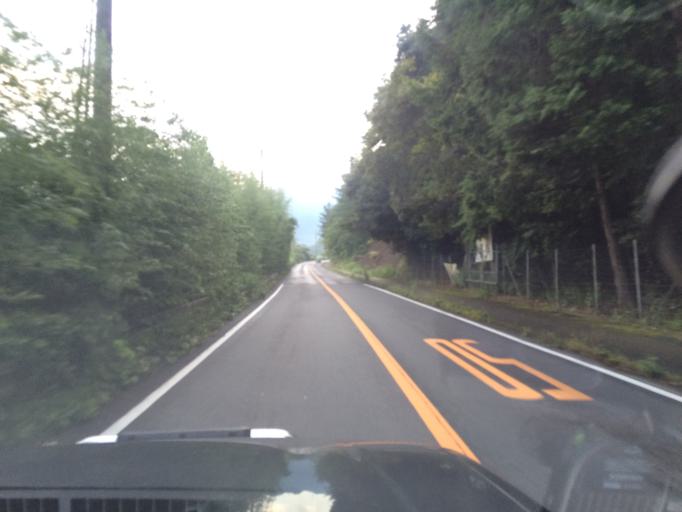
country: JP
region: Hyogo
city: Nishiwaki
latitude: 35.0942
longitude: 134.9975
